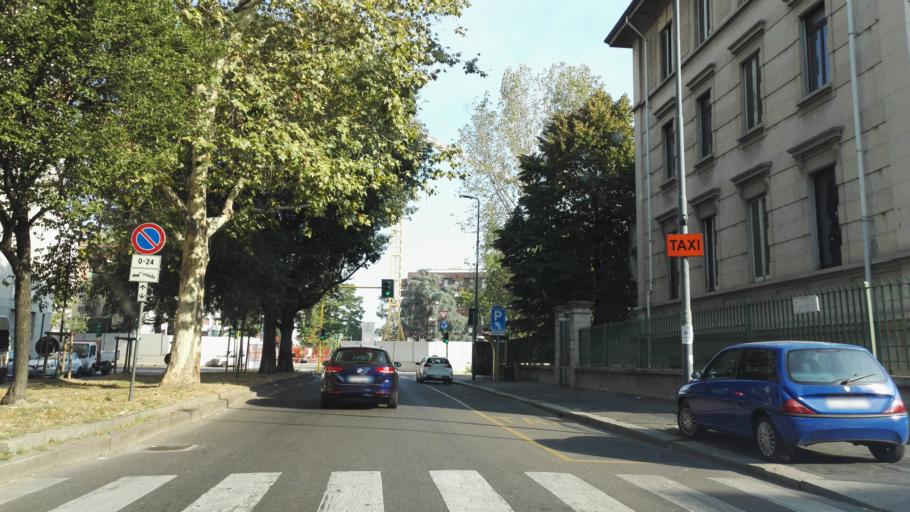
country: IT
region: Lombardy
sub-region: Citta metropolitana di Milano
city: Romano Banco
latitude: 45.4508
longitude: 9.1432
